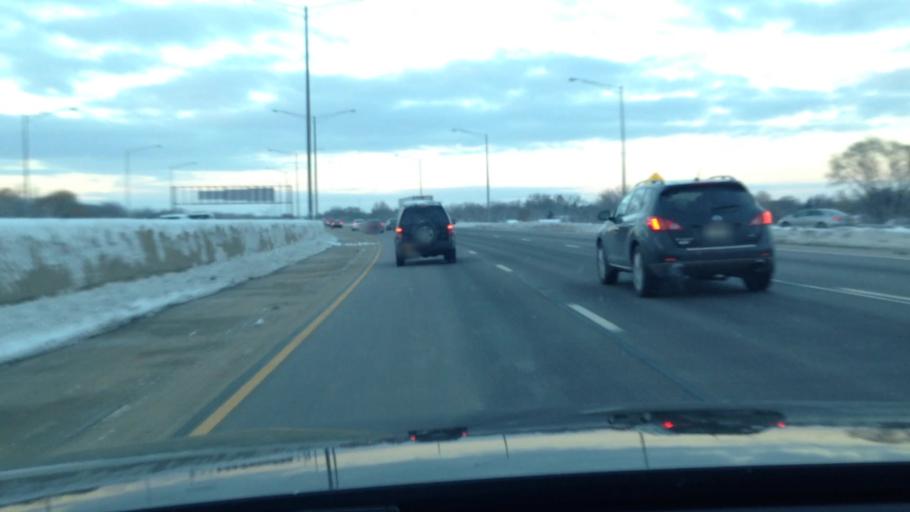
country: US
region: Illinois
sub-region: Cook County
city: Rolling Meadows
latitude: 42.1118
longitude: -88.0029
